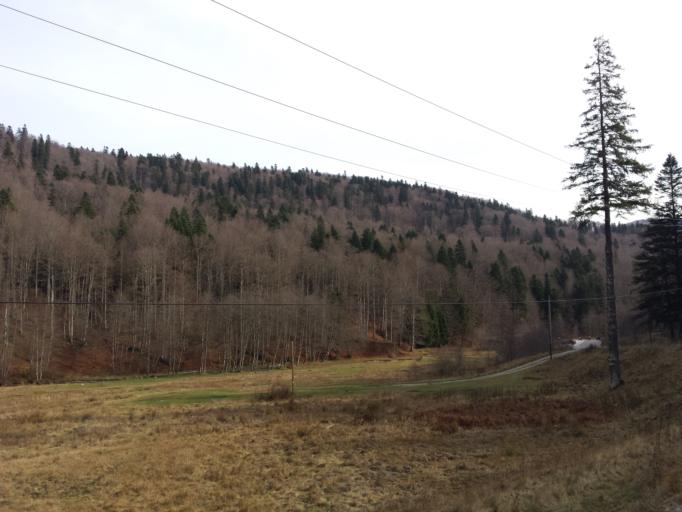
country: RO
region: Prahova
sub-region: Oras Azuga
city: Azuga
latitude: 45.4304
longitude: 25.5320
